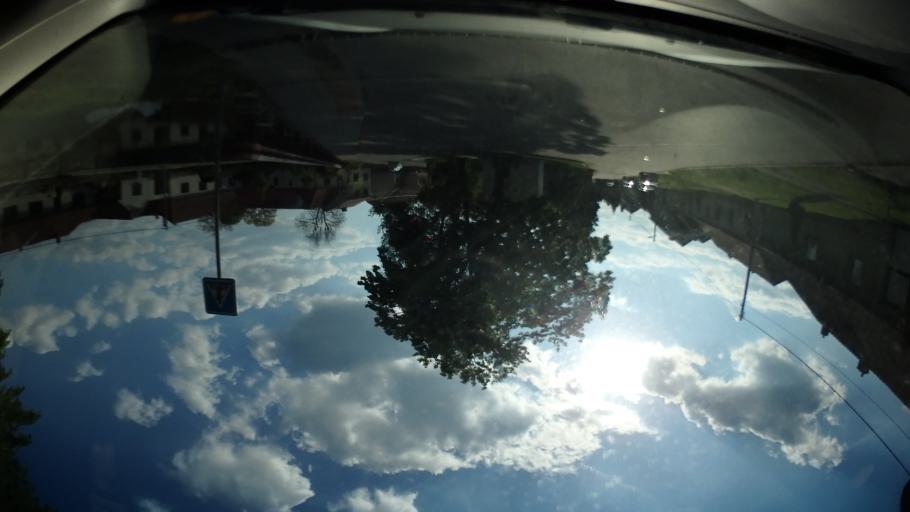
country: CZ
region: Vysocina
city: Budisov
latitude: 49.2938
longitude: 15.9861
